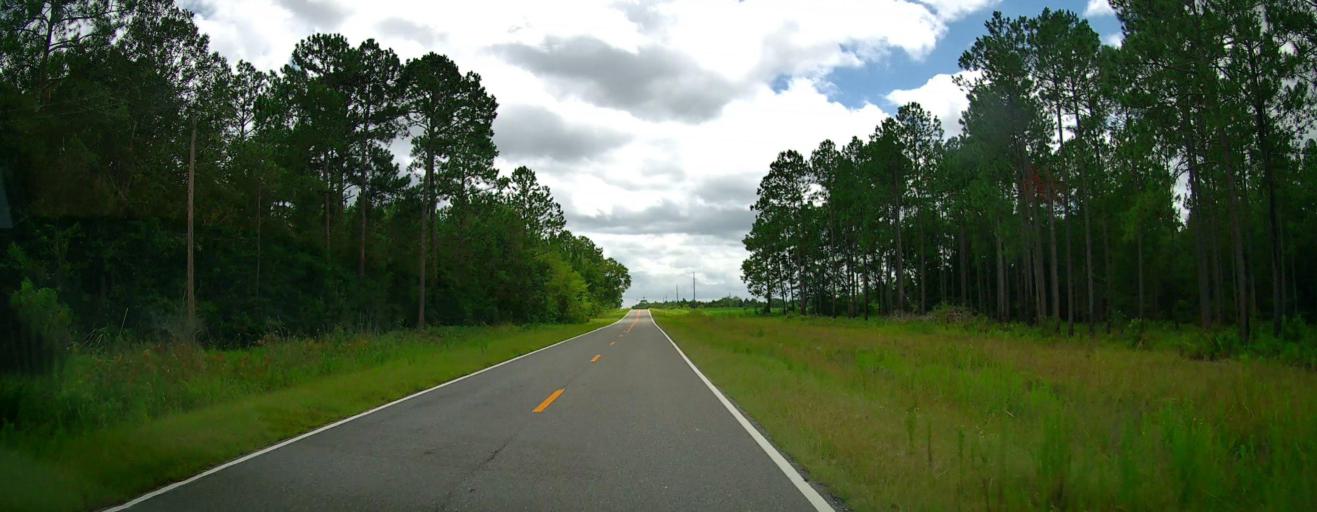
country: US
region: Georgia
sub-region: Turner County
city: Ashburn
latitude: 31.6805
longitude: -83.4763
